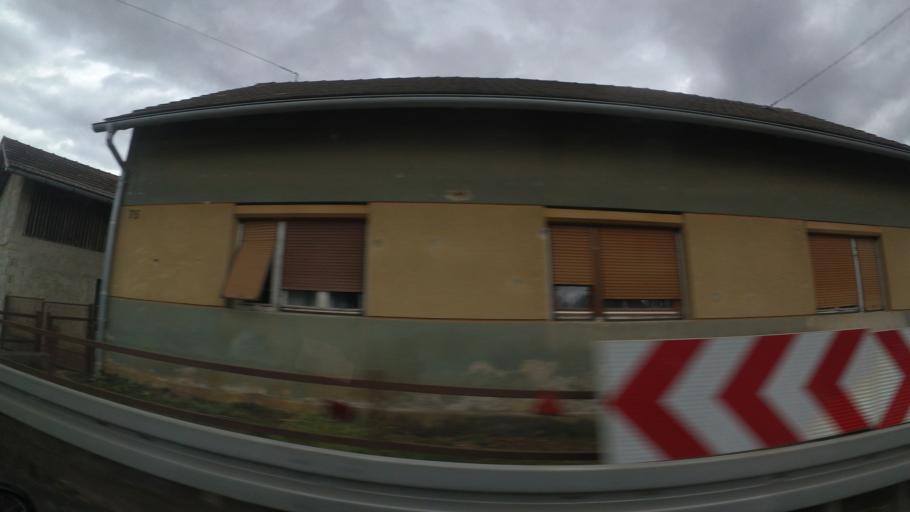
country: HR
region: Karlovacka
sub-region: Grad Karlovac
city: Karlovac
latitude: 45.4378
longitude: 15.5525
